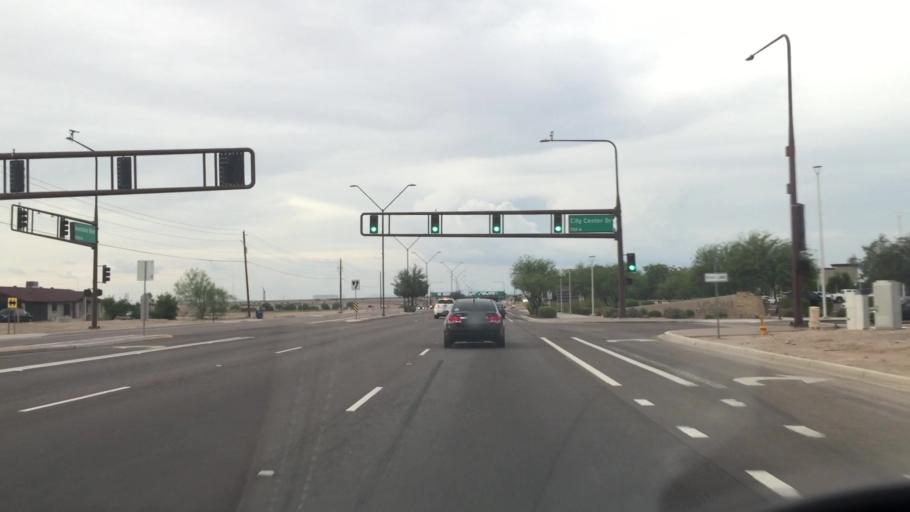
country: US
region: Arizona
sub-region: Maricopa County
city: Avondale
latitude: 33.4533
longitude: -112.3063
